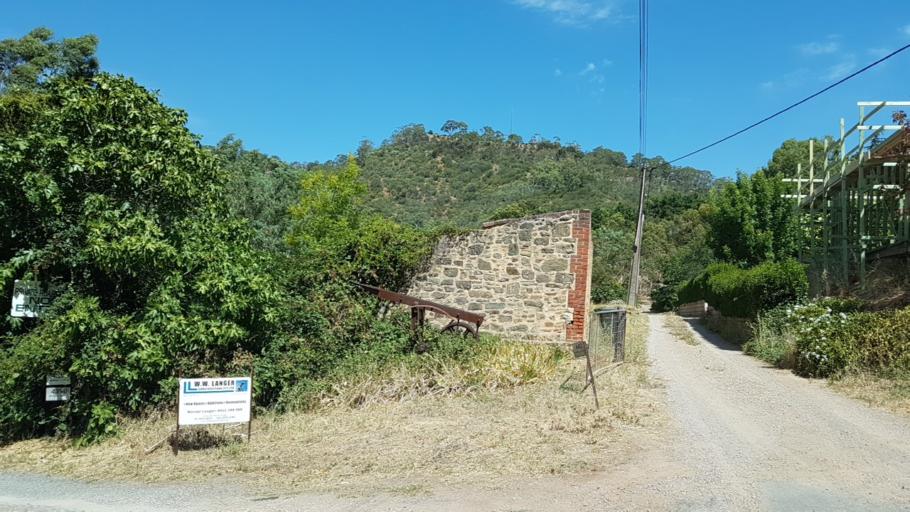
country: AU
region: South Australia
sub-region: Burnside
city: Mount Osmond
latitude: -34.9932
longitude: 138.6544
